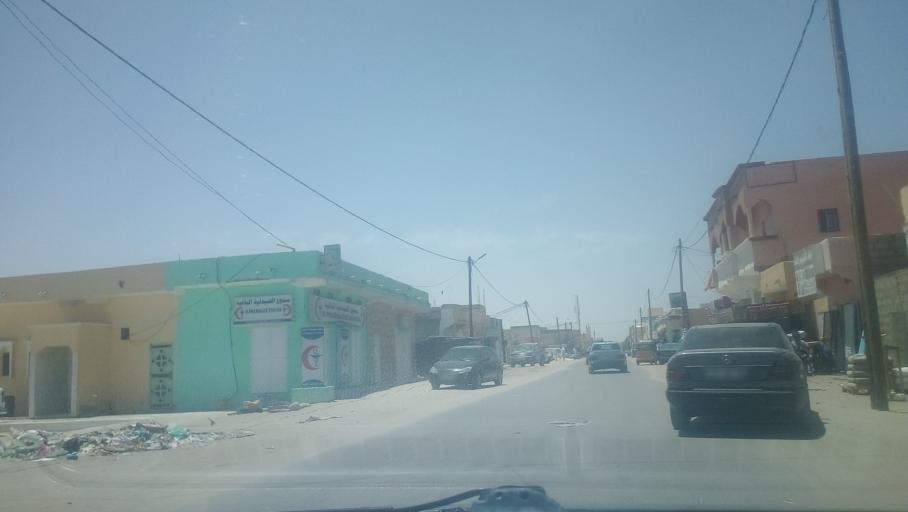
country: MR
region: Nouakchott
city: Nouakchott
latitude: 18.0656
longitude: -15.9590
